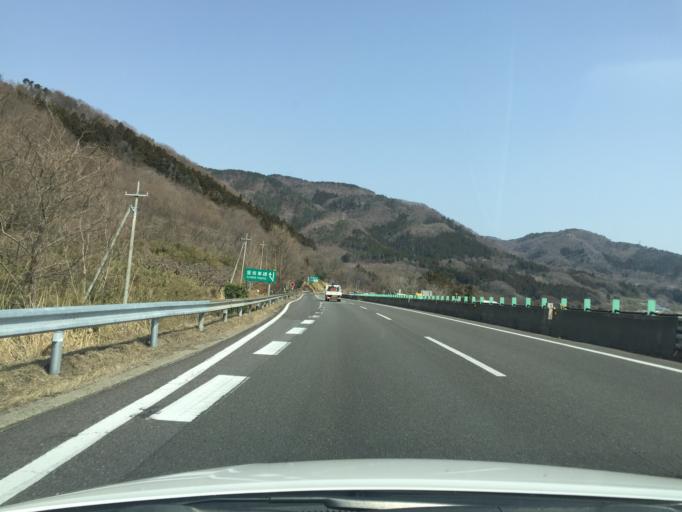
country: JP
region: Fukushima
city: Yanagawamachi-saiwaicho
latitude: 37.8953
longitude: 140.5696
